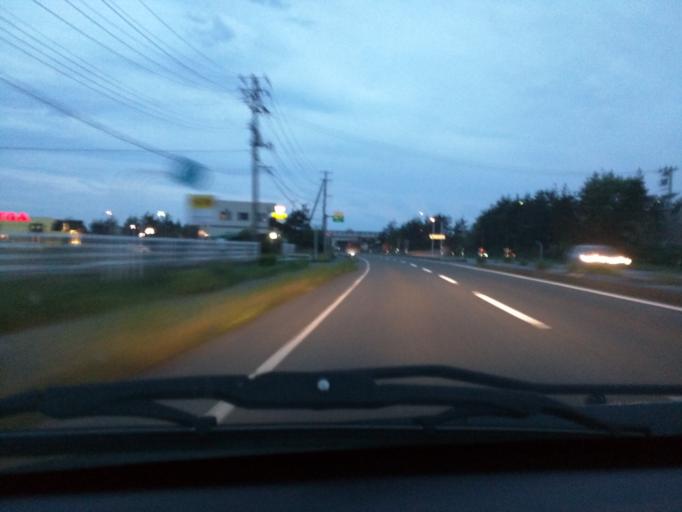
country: JP
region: Niigata
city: Kashiwazaki
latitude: 37.3602
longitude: 138.5909
